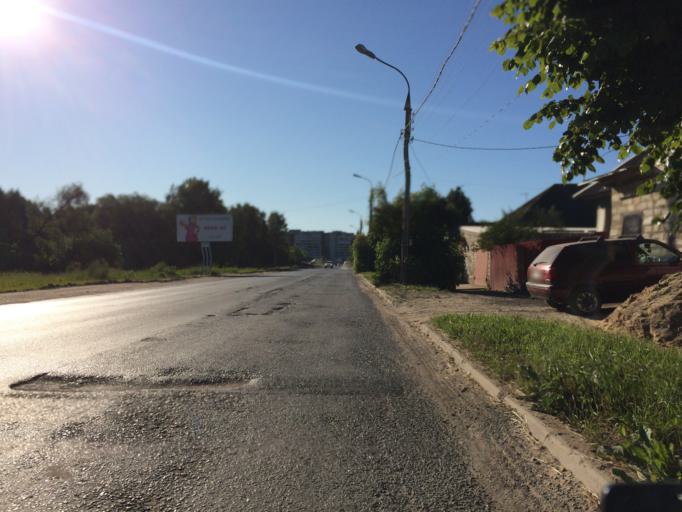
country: RU
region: Mariy-El
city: Medvedevo
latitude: 56.6530
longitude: 47.8435
